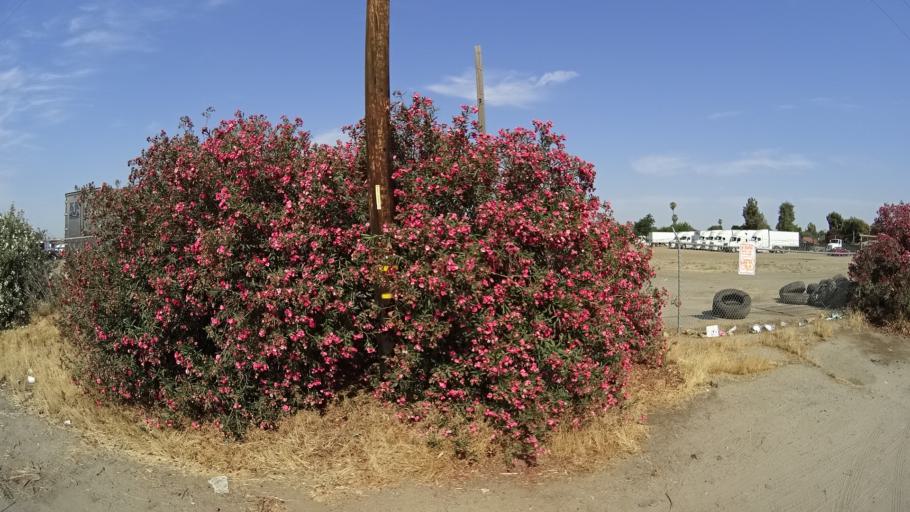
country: US
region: California
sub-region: Fresno County
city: Fresno
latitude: 36.7458
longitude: -119.8176
